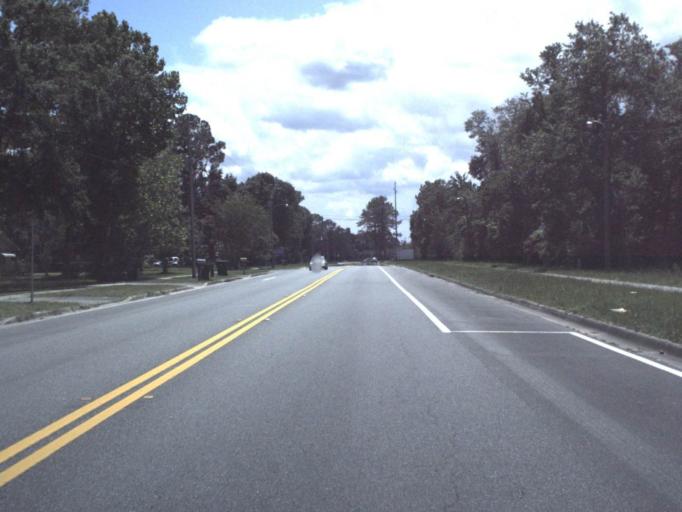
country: US
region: Florida
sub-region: Bradford County
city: Starke
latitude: 29.9555
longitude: -82.1142
